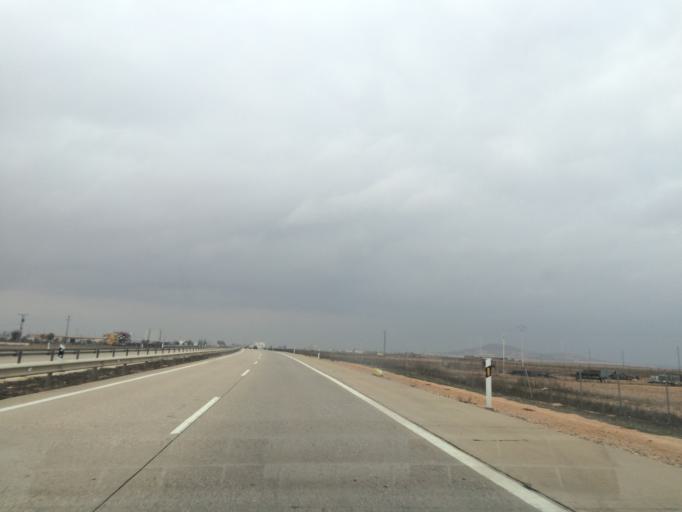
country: ES
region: Castille-La Mancha
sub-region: Province of Toledo
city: Madridejos
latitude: 39.4915
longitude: -3.5262
